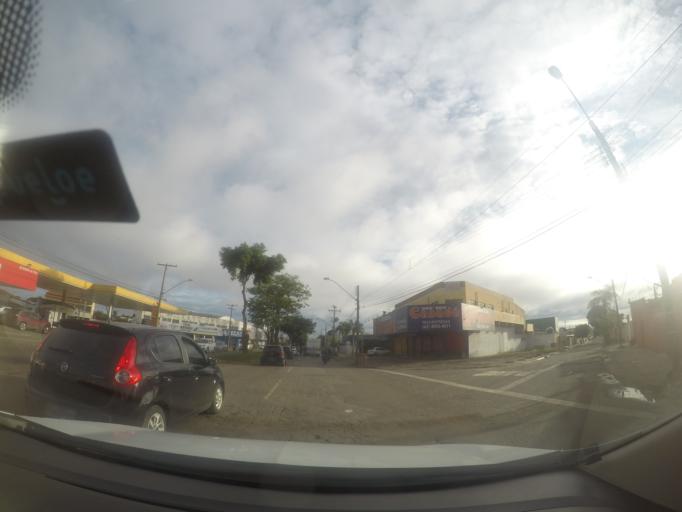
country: BR
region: Goias
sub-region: Goiania
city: Goiania
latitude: -16.6875
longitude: -49.3147
